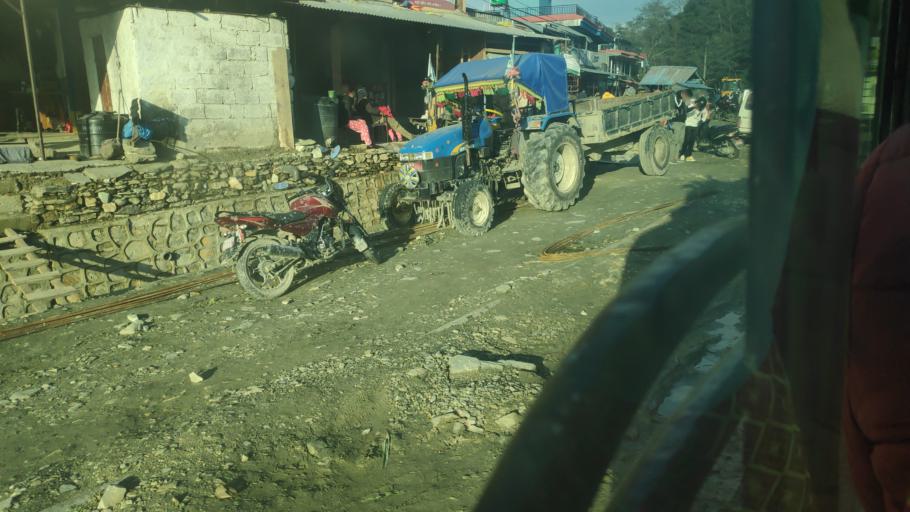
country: NP
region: Western Region
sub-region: Gandaki Zone
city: Pokhara
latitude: 28.2816
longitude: 83.8665
